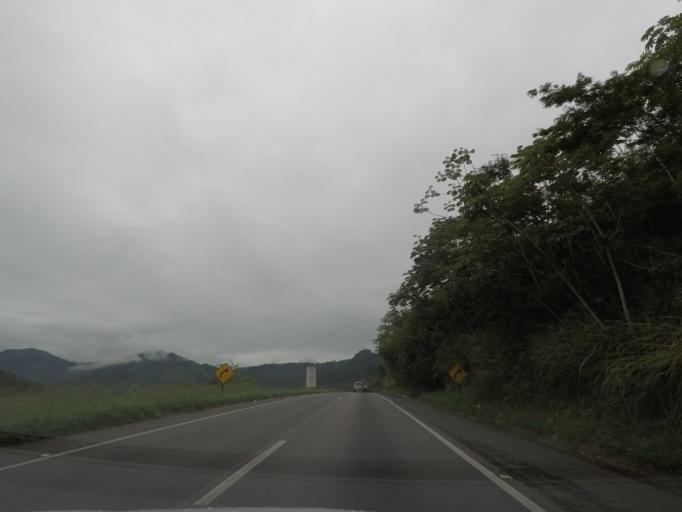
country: BR
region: Sao Paulo
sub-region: Cajati
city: Cajati
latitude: -24.7834
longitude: -48.2037
